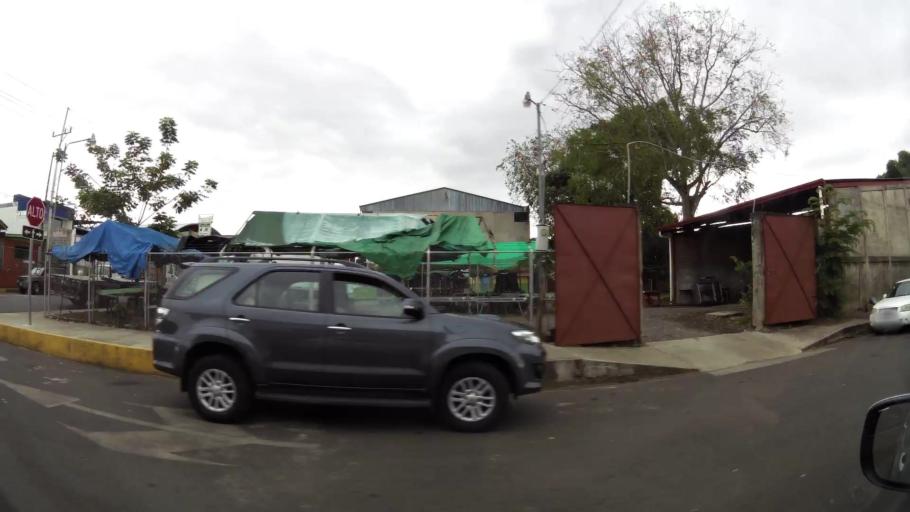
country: CR
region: Alajuela
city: Orotina
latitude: 9.9133
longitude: -84.5255
